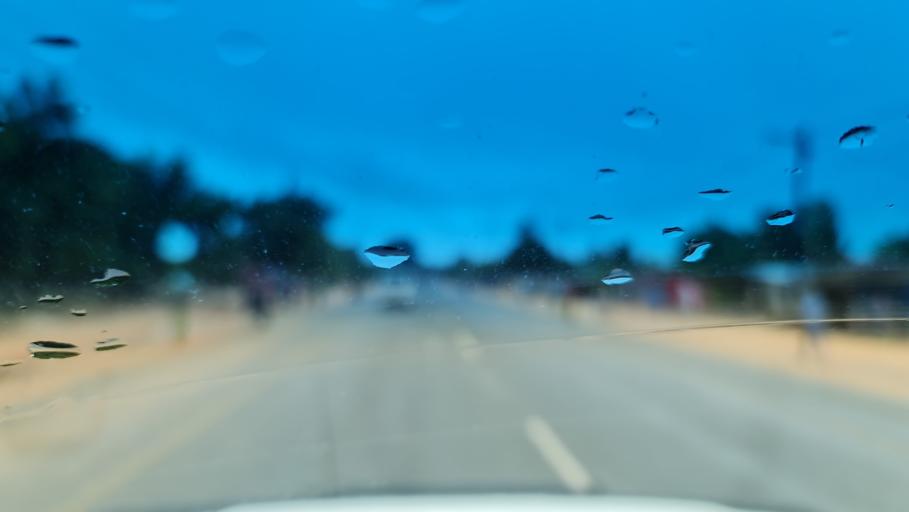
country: MZ
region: Nampula
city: Nampula
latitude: -15.1456
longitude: 39.2974
